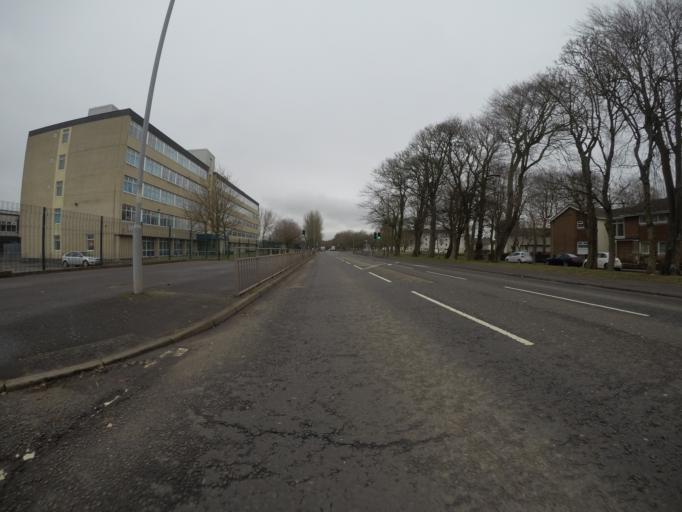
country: GB
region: Scotland
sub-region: North Ayrshire
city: Irvine
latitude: 55.6277
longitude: -4.6742
